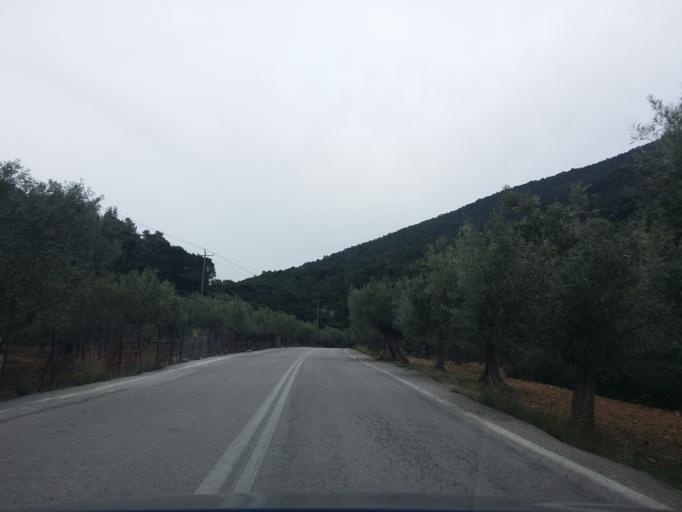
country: GR
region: Attica
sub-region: Nomarchia Dytikis Attikis
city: Vilia
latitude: 38.1428
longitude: 23.2557
